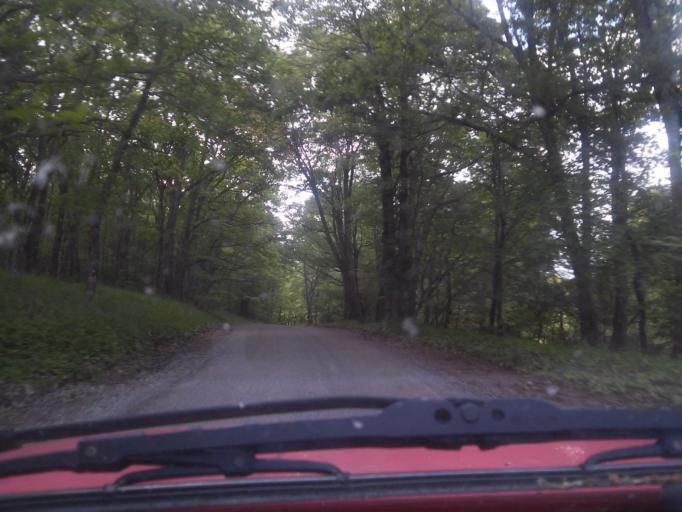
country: US
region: Virginia
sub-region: Giles County
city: Pembroke
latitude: 37.3693
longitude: -80.5308
